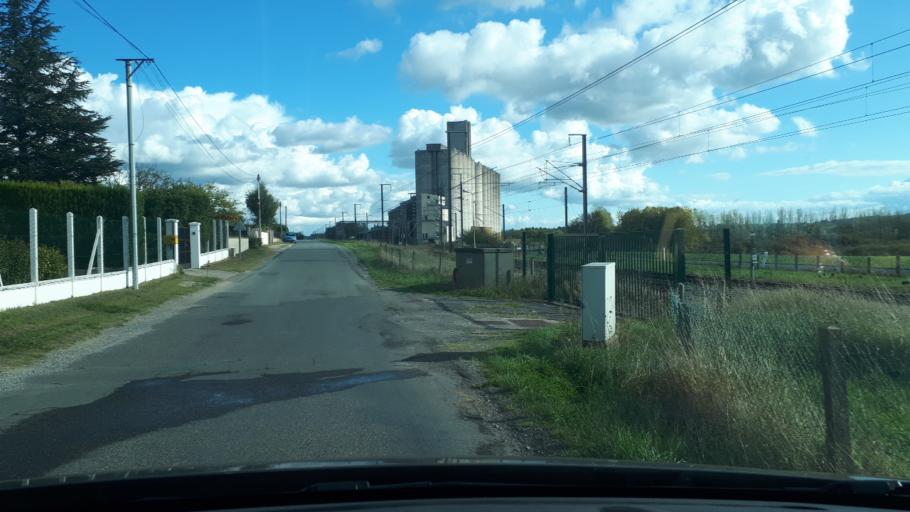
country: FR
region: Centre
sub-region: Departement du Loir-et-Cher
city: Mareuil-sur-Cher
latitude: 47.2979
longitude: 1.3600
